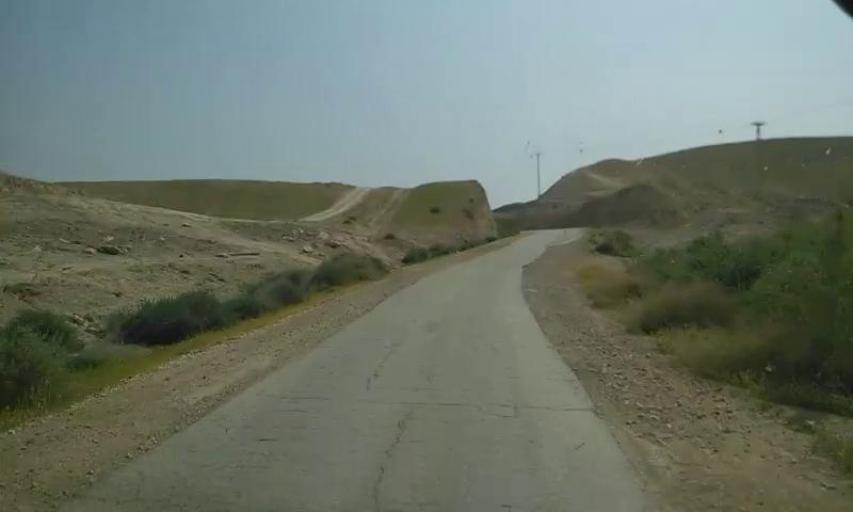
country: PS
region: West Bank
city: Jericho
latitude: 31.7927
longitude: 35.4274
